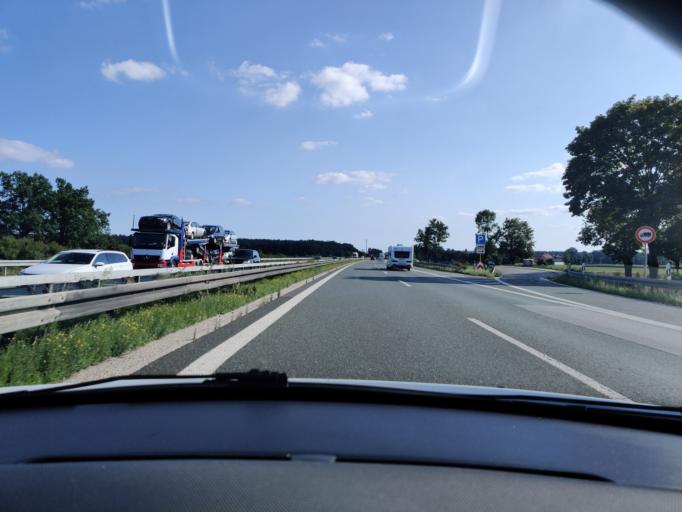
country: DE
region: Bavaria
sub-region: Upper Palatinate
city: Schwarzenfeld
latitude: 49.3693
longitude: 12.1526
